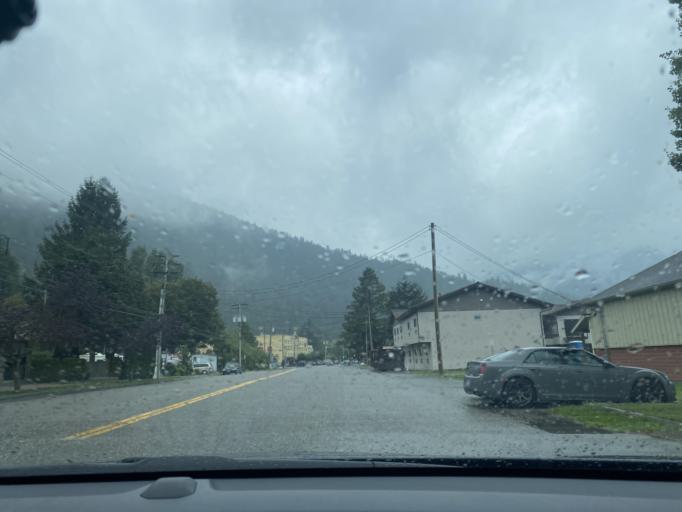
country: CA
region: British Columbia
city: Agassiz
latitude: 49.3026
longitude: -121.7828
